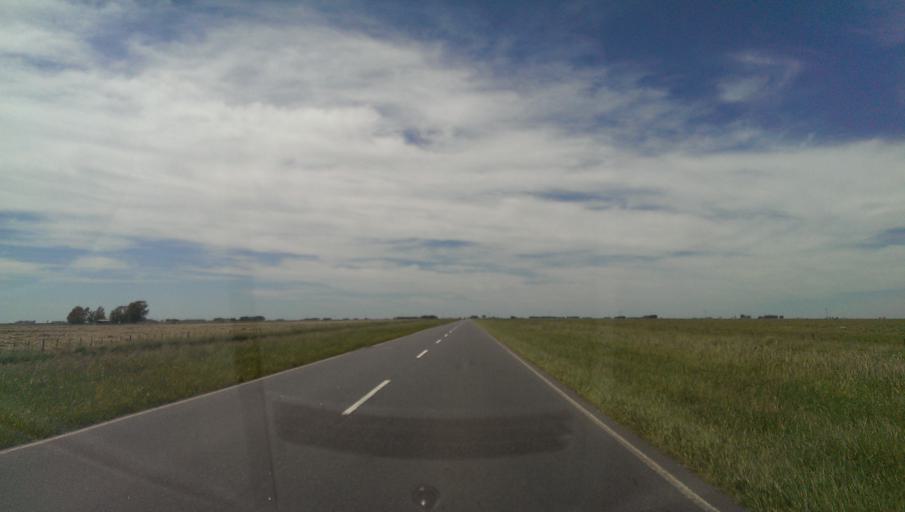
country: AR
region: Buenos Aires
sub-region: Partido de Laprida
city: Laprida
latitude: -37.2406
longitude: -60.7659
